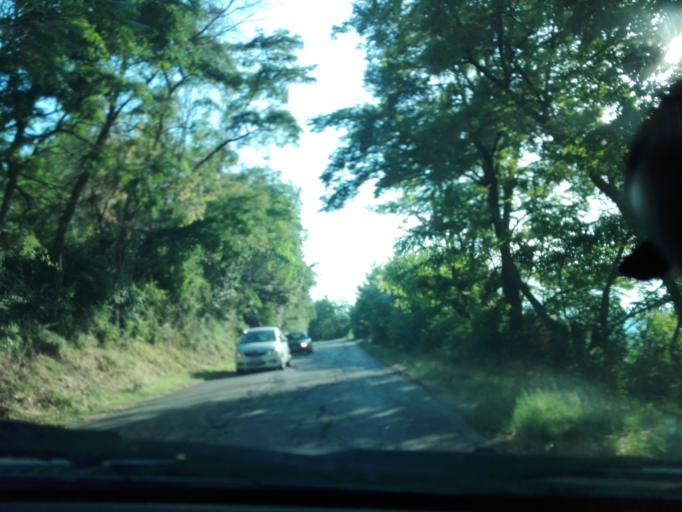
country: IT
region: Abruzzo
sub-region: Provincia di Pescara
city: Cappelle sul Tavo
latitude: 42.4619
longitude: 14.1029
